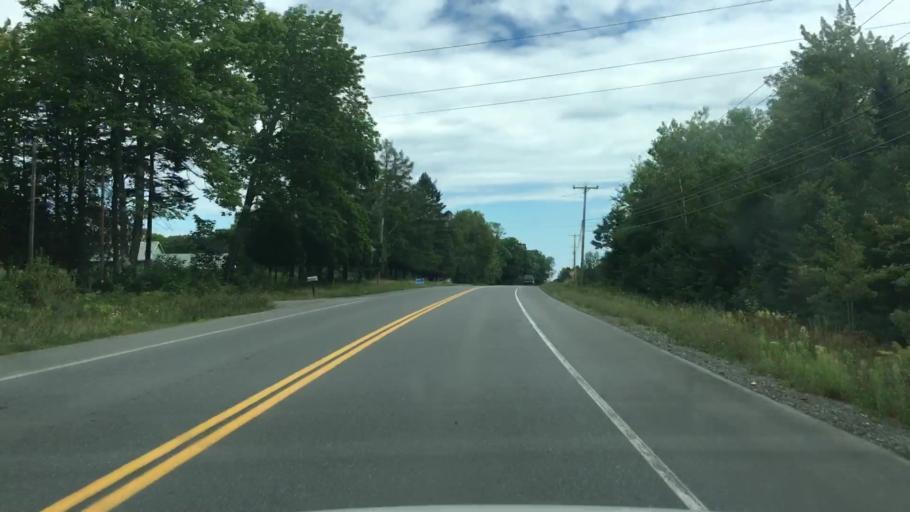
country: US
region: Maine
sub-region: Piscataquis County
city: Milo
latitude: 45.2436
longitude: -69.0151
